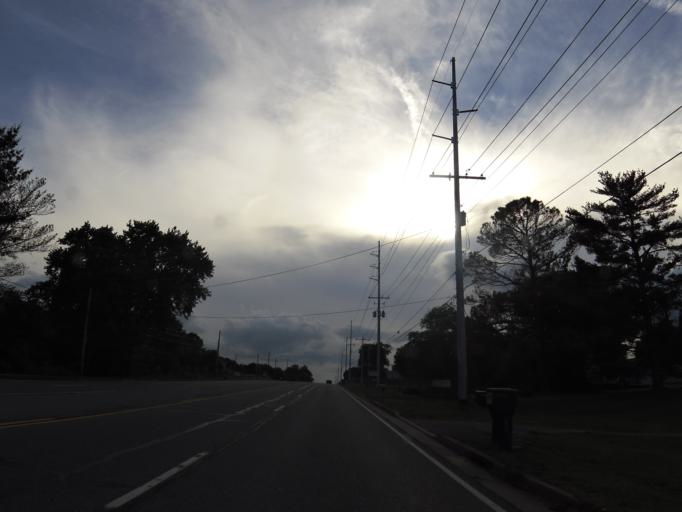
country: US
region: Tennessee
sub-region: Blount County
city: Eagleton Village
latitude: 35.7571
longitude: -83.9058
